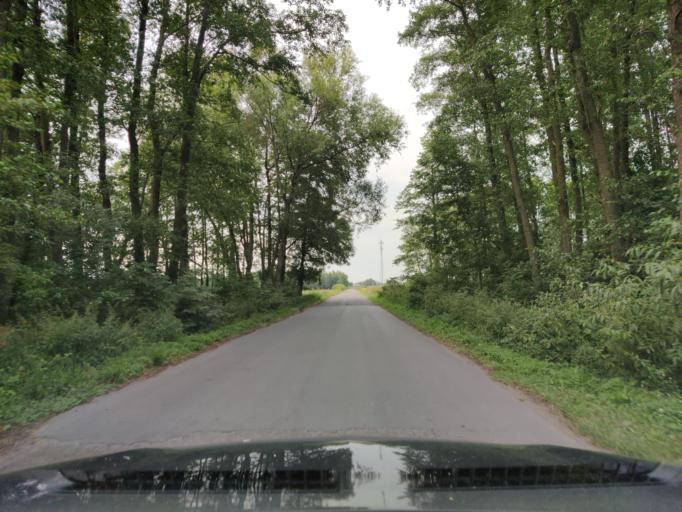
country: PL
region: Masovian Voivodeship
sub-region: Powiat pultuski
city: Obryte
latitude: 52.7304
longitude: 21.2459
